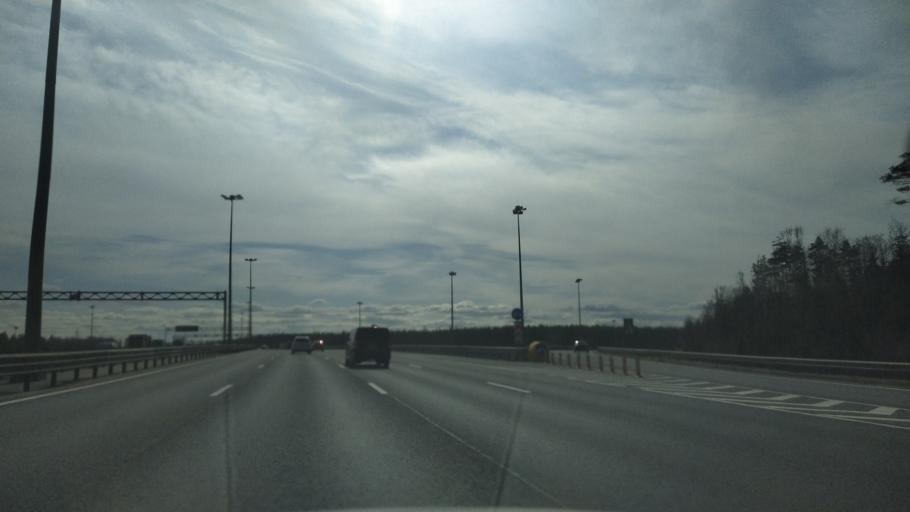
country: RU
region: St.-Petersburg
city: Krasnogvargeisky
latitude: 59.9490
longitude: 30.5430
